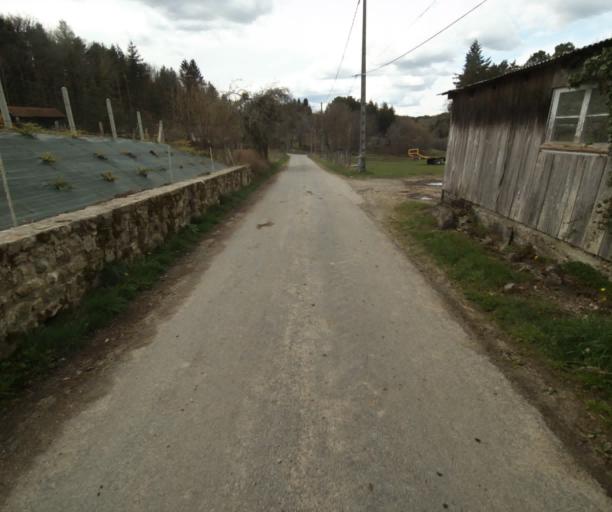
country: FR
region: Limousin
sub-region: Departement de la Correze
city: Argentat
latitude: 45.1925
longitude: 1.9584
